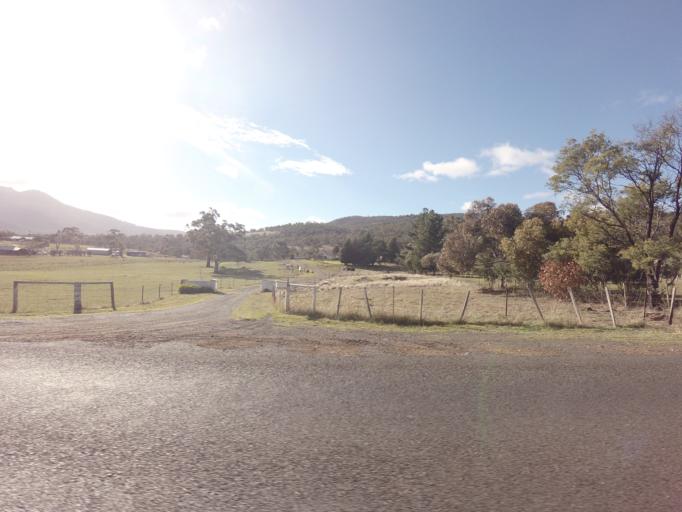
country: AU
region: Tasmania
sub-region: Derwent Valley
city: New Norfolk
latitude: -42.7896
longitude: 147.1218
